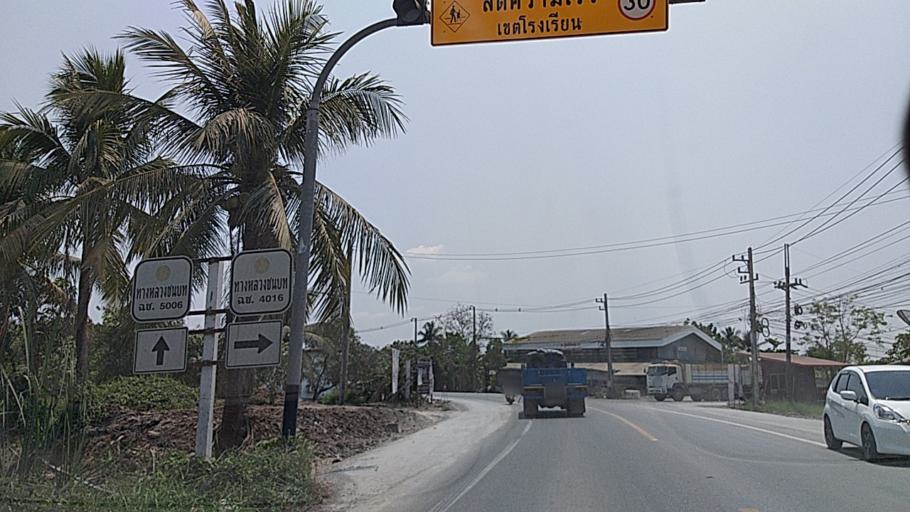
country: TH
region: Chachoengsao
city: Bang Nam Priao
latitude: 13.9420
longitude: 100.9787
